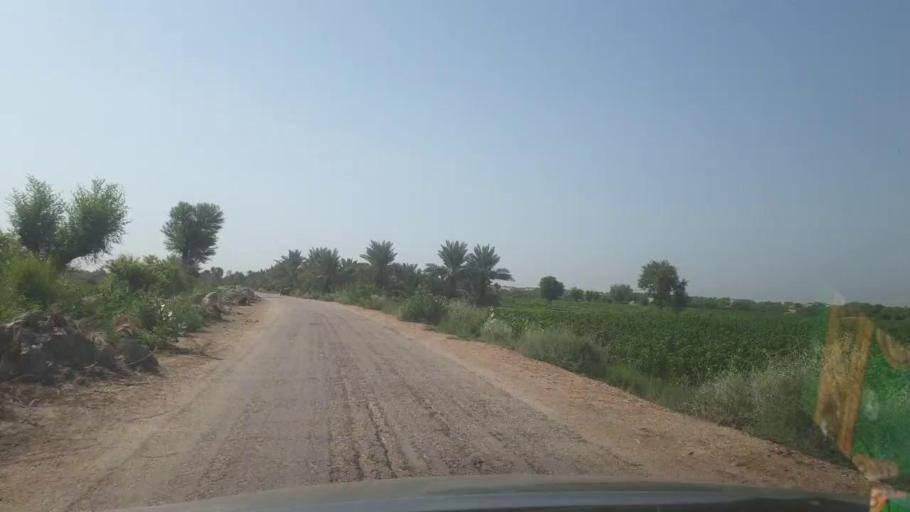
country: PK
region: Sindh
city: Rohri
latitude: 27.4661
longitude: 69.0381
